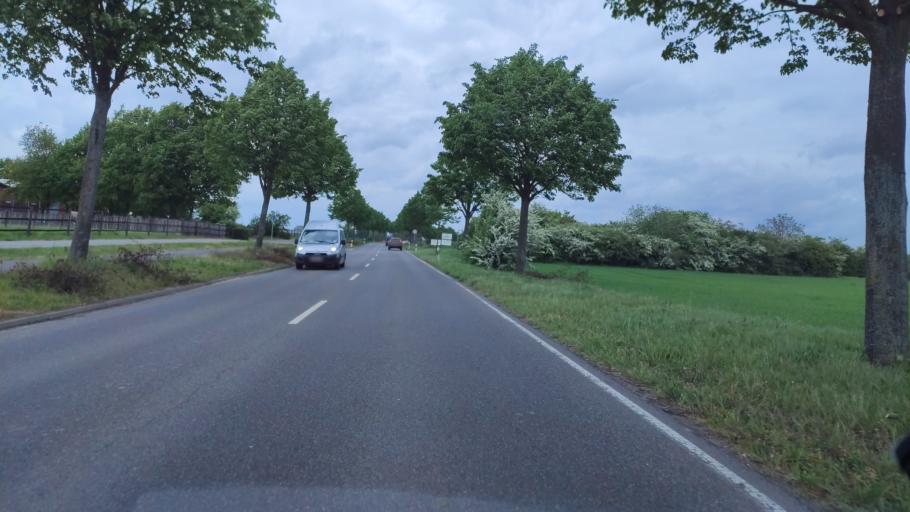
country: DE
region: North Rhine-Westphalia
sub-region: Regierungsbezirk Dusseldorf
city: Kaarst
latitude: 51.2063
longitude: 6.6197
